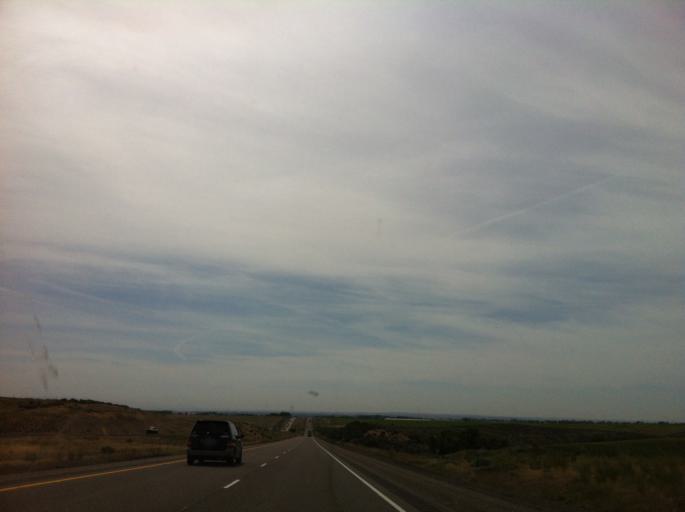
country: US
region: Oregon
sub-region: Malheur County
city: Ontario
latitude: 44.1051
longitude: -117.0473
